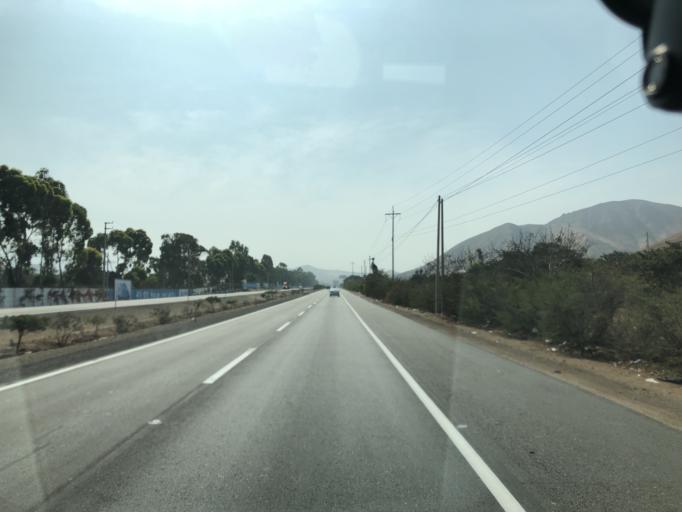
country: PE
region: Lima
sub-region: Provincia de Canete
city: Chilca
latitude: -12.5793
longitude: -76.6805
